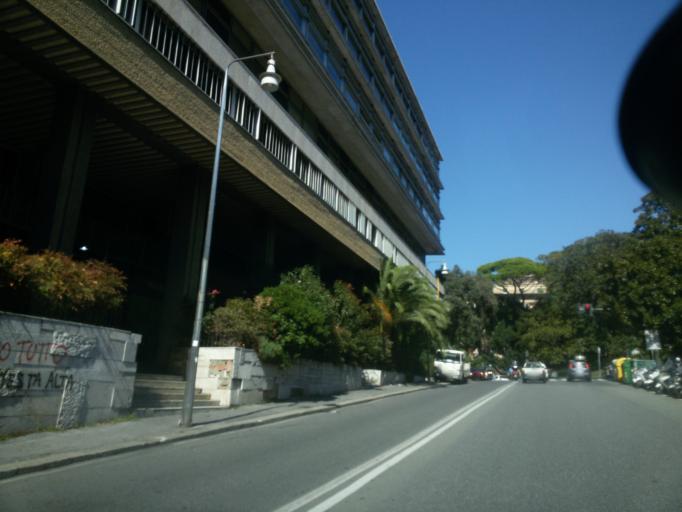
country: IT
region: Liguria
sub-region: Provincia di Genova
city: San Teodoro
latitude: 44.4087
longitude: 8.9384
